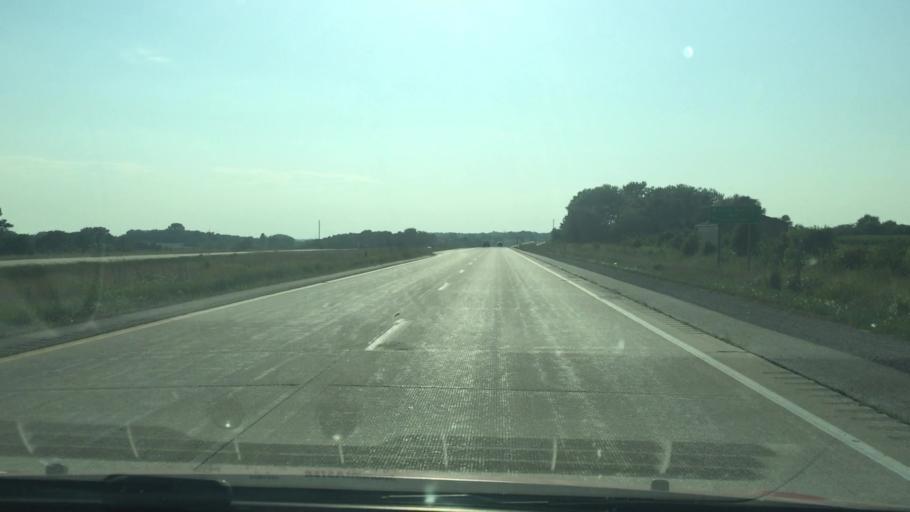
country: US
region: Iowa
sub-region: Scott County
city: Blue Grass
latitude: 41.5130
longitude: -90.7898
